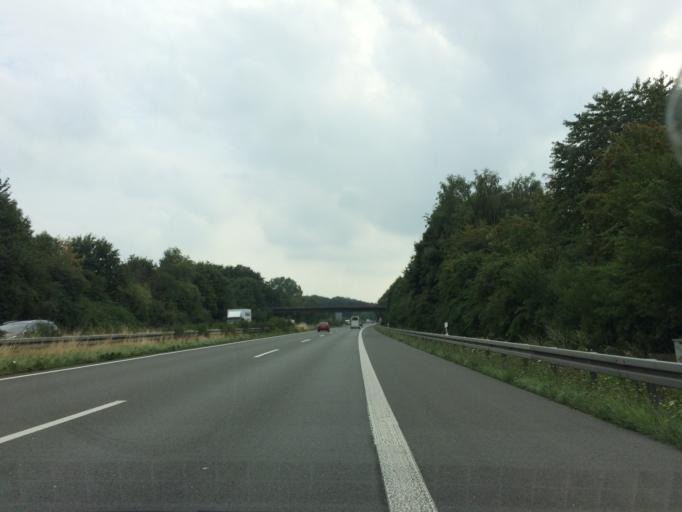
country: DE
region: North Rhine-Westphalia
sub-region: Regierungsbezirk Munster
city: Klein Reken
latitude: 51.7539
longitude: 6.9651
